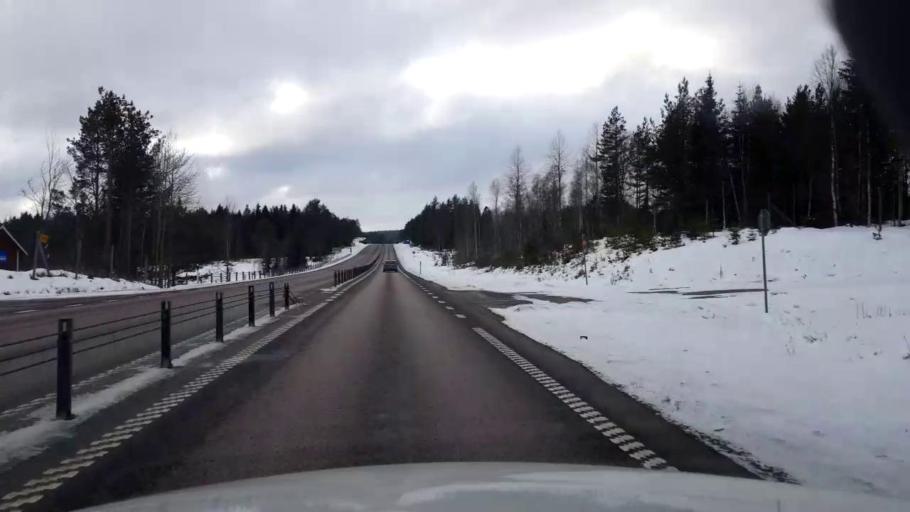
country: SE
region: Gaevleborg
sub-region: Hudiksvalls Kommun
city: Hudiksvall
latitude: 61.8089
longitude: 17.1845
